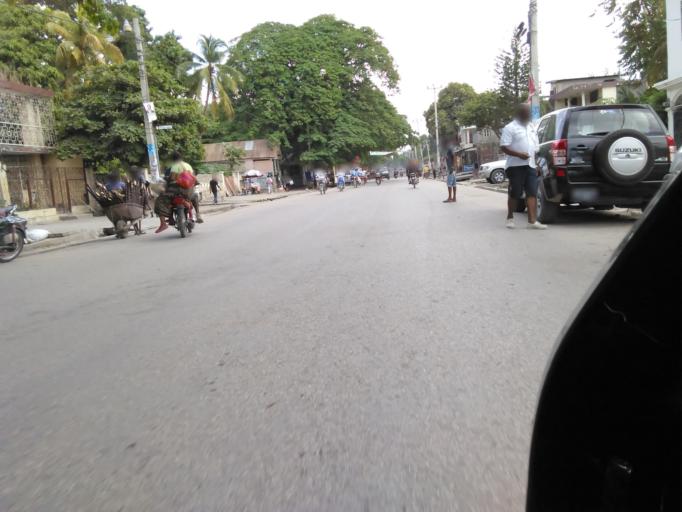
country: HT
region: Artibonite
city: Saint-Marc
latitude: 19.1066
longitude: -72.6962
